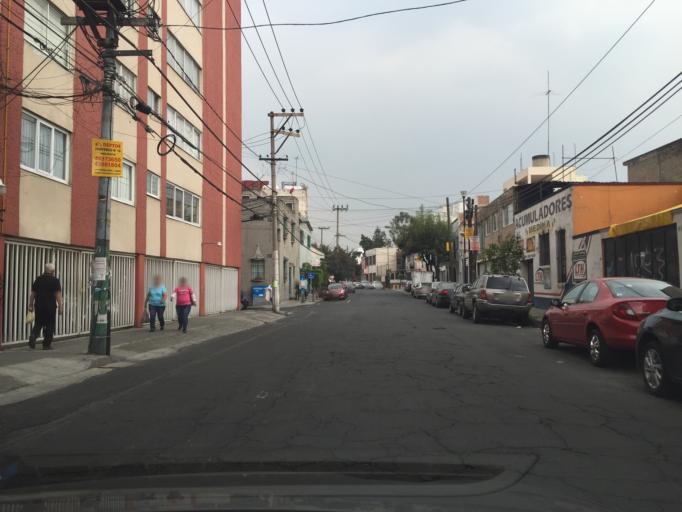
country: MX
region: Mexico City
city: Alvaro Obregon
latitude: 19.3773
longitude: -99.1895
